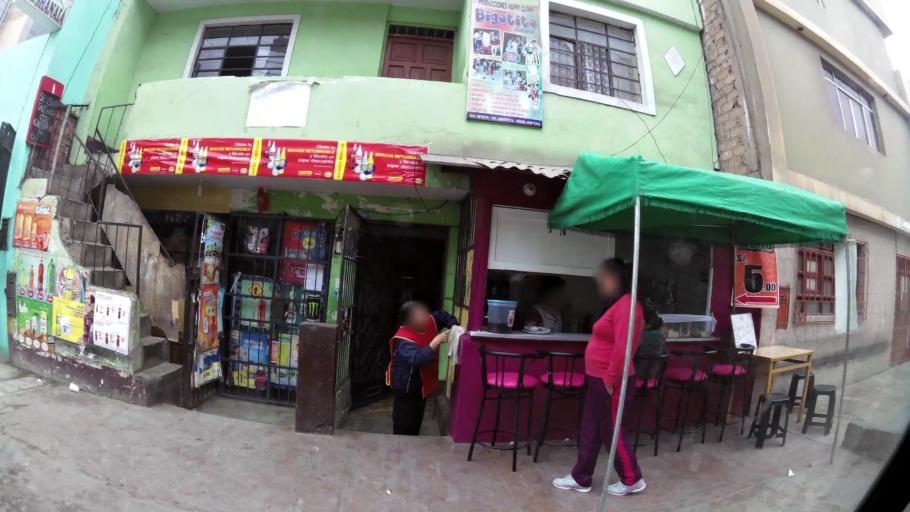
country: PE
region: Callao
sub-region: Callao
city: Callao
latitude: -12.0463
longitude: -77.1107
